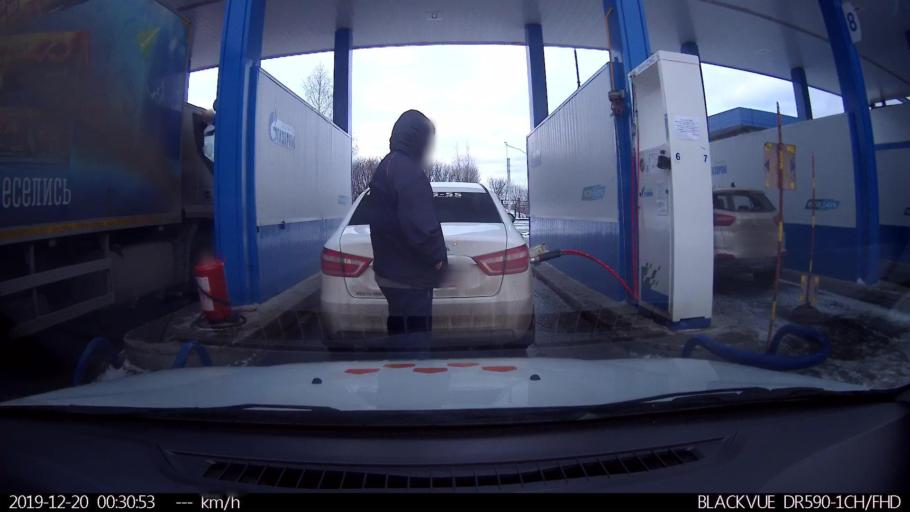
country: RU
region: Vladimir
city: Yur'yev-Pol'skiy
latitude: 56.5121
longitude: 39.6527
